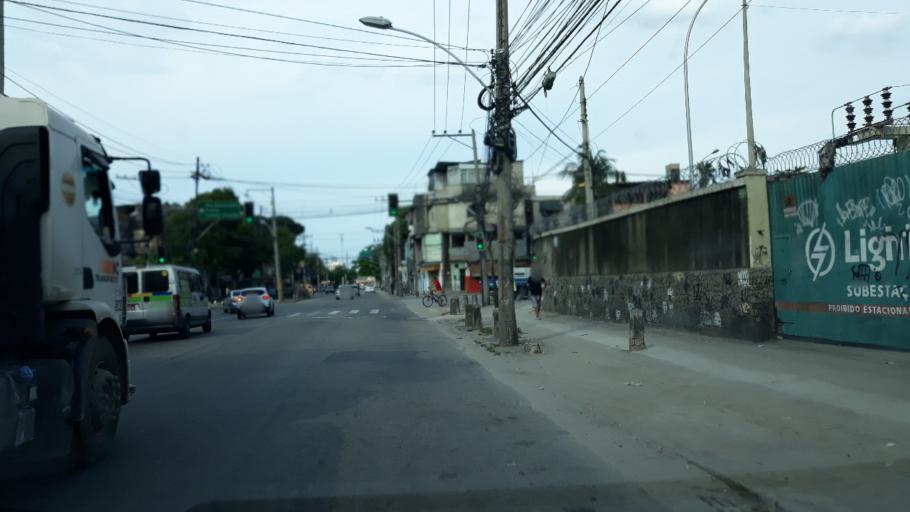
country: BR
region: Rio de Janeiro
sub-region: Rio De Janeiro
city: Rio de Janeiro
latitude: -22.8892
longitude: -43.2328
